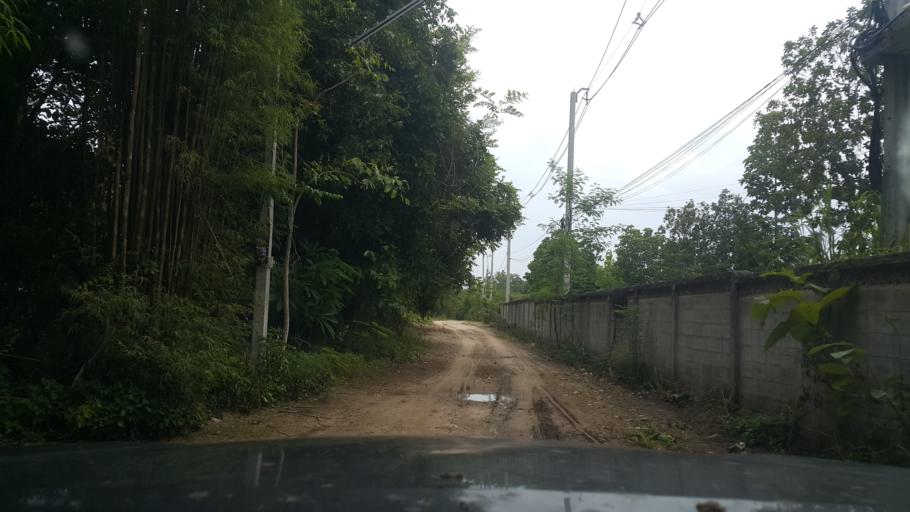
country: TH
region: Chiang Mai
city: San Pa Tong
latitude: 18.6476
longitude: 98.8449
